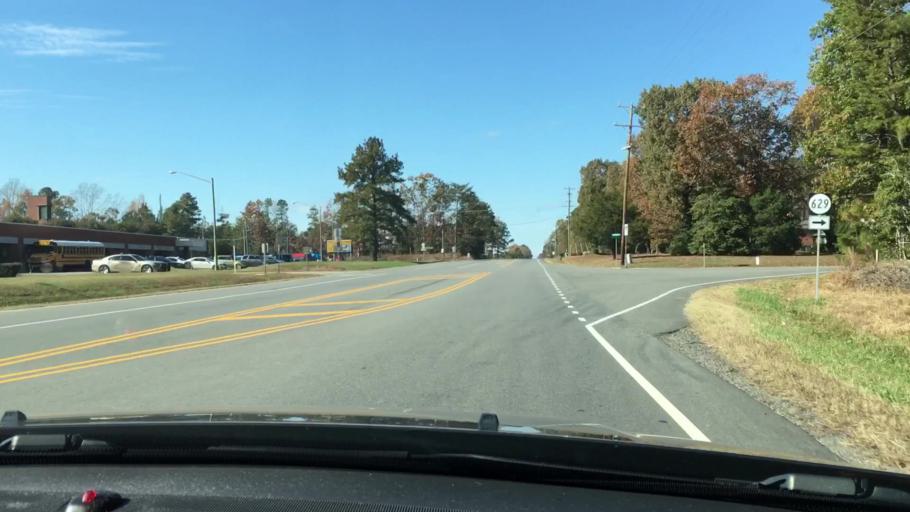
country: US
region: Virginia
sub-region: King William County
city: King William
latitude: 37.6952
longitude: -77.0344
